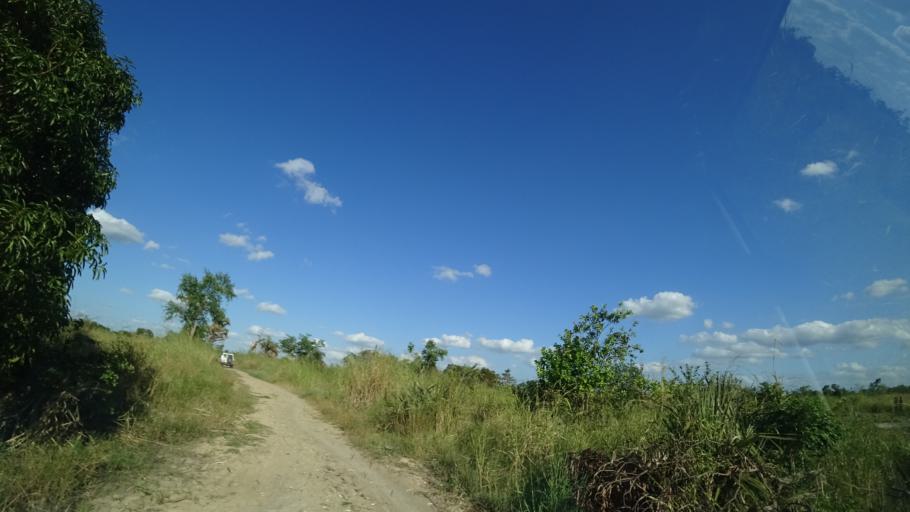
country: MZ
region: Sofala
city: Dondo
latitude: -19.3476
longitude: 34.5818
